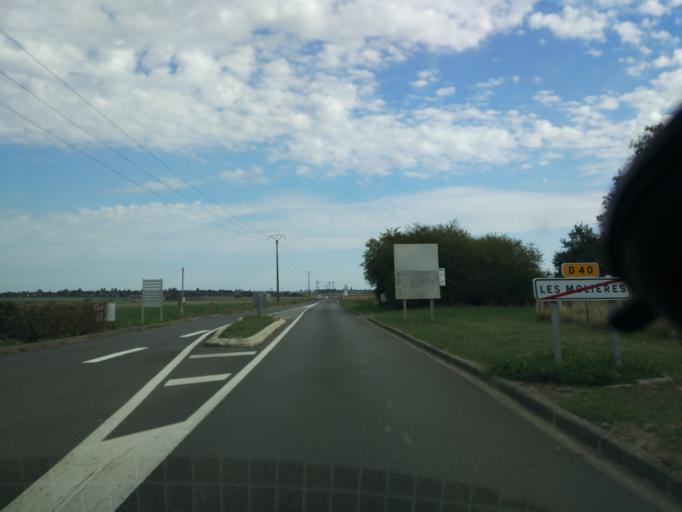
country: FR
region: Ile-de-France
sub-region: Departement de l'Essonne
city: Les Molieres
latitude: 48.6721
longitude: 2.0803
